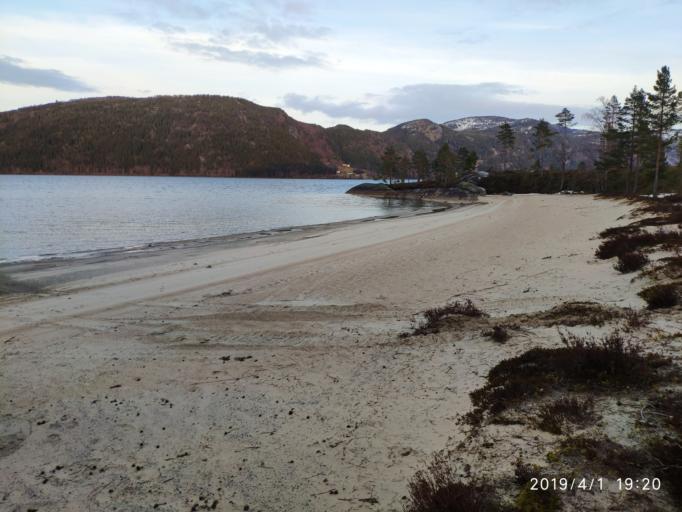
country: NO
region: Telemark
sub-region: Nissedal
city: Treungen
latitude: 59.1257
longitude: 8.4773
